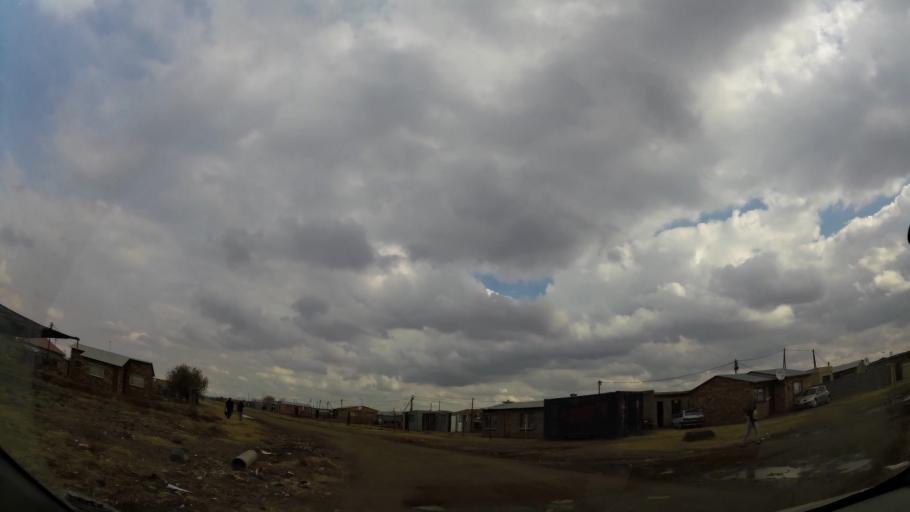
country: ZA
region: Orange Free State
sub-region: Fezile Dabi District Municipality
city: Sasolburg
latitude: -26.8583
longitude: 27.8930
